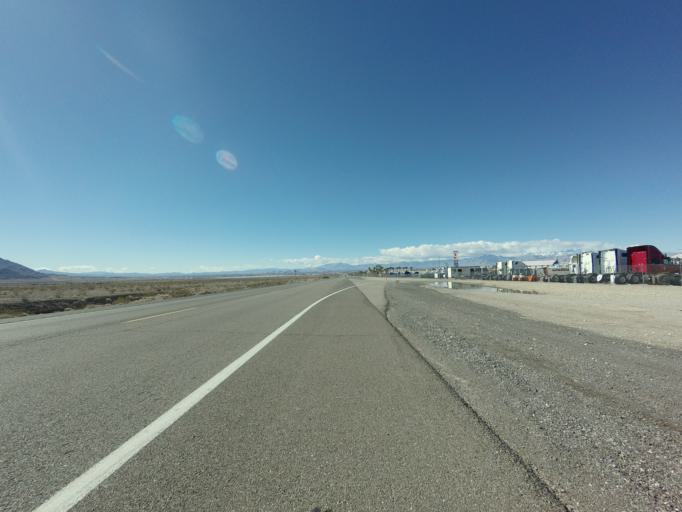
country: US
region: Nevada
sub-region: Clark County
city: Nellis Air Force Base
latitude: 36.2733
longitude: -114.9984
